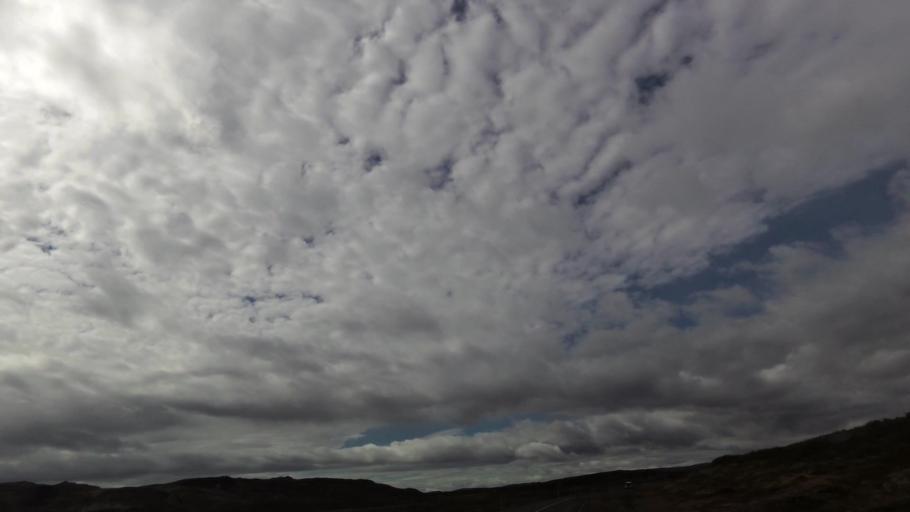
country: IS
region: West
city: Stykkisholmur
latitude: 65.5347
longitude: -22.0902
